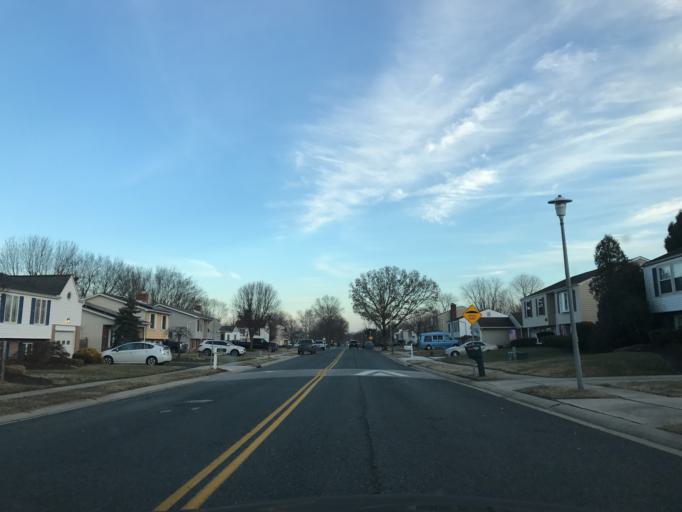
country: US
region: Maryland
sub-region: Harford County
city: Joppatowne
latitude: 39.4103
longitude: -76.3644
